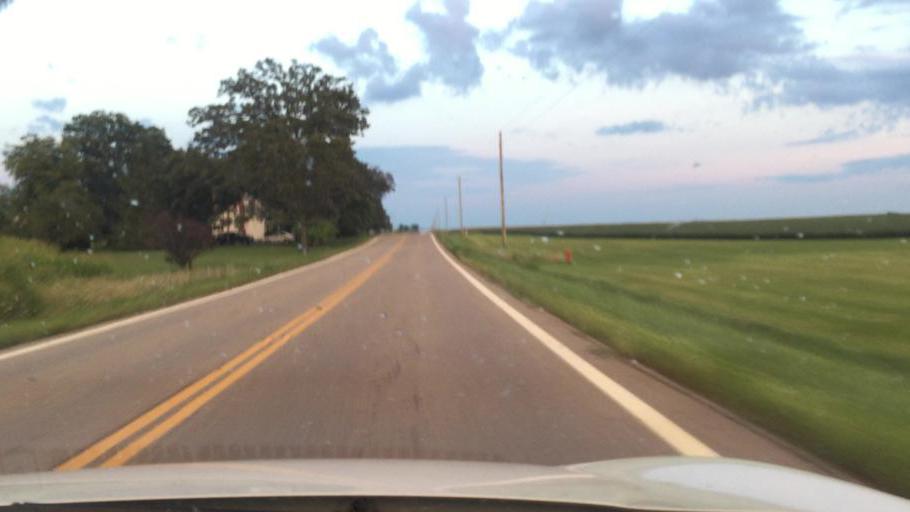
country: US
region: Ohio
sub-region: Madison County
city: Choctaw Lake
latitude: 40.0259
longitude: -83.4804
